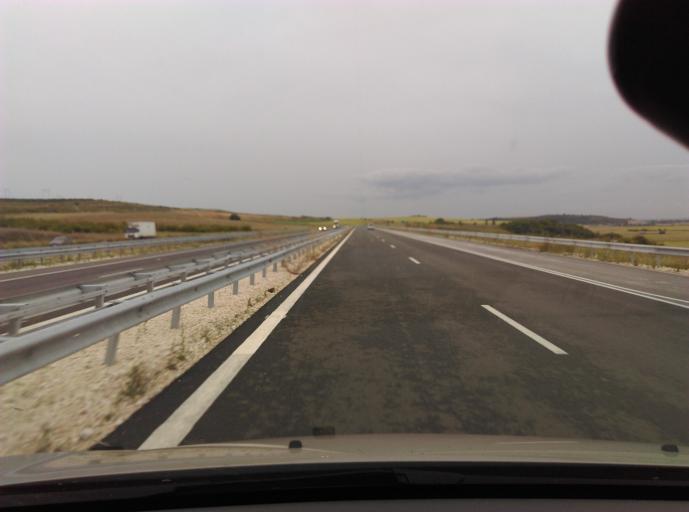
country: BG
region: Stara Zagora
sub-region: Obshtina Chirpan
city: Chirpan
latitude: 42.1189
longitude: 25.3900
